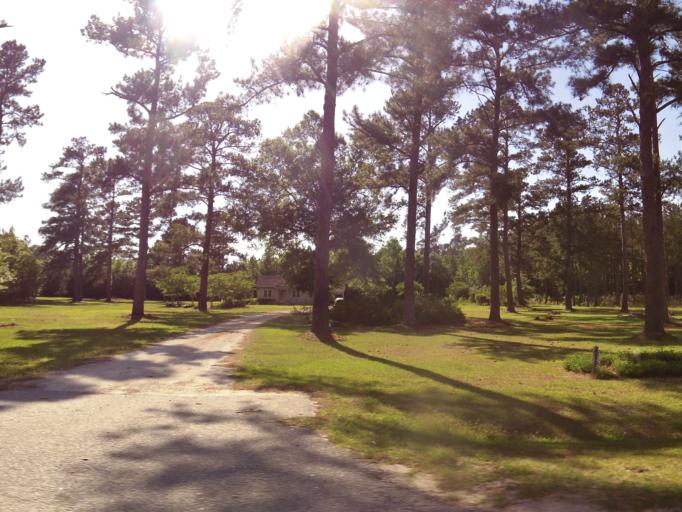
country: US
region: South Carolina
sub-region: Allendale County
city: Allendale
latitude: 33.0858
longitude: -81.2090
